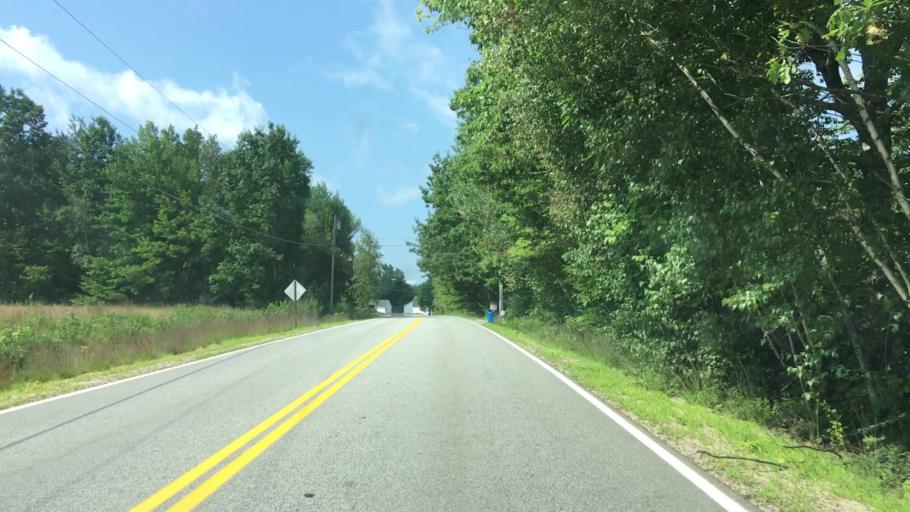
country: US
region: Maine
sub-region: Cumberland County
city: Raymond
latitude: 43.9503
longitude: -70.4301
